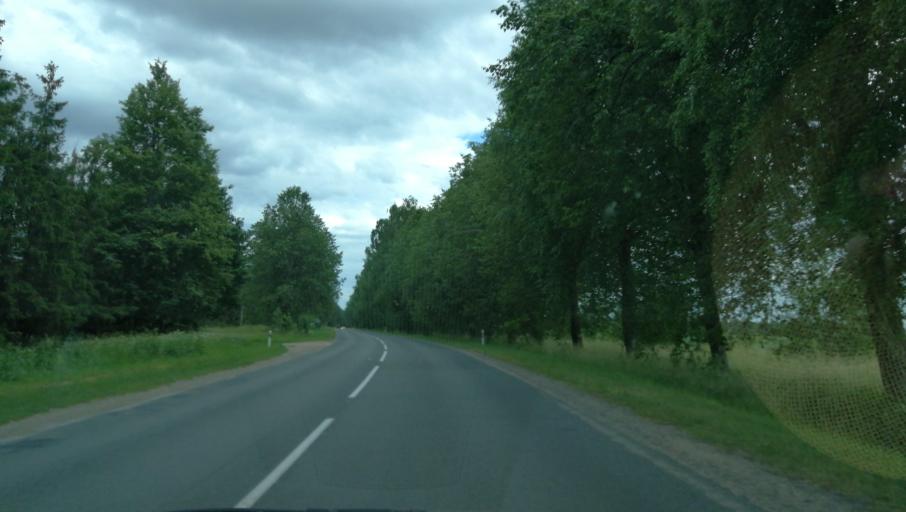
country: LV
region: Rujienas
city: Rujiena
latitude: 57.8803
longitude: 25.3570
